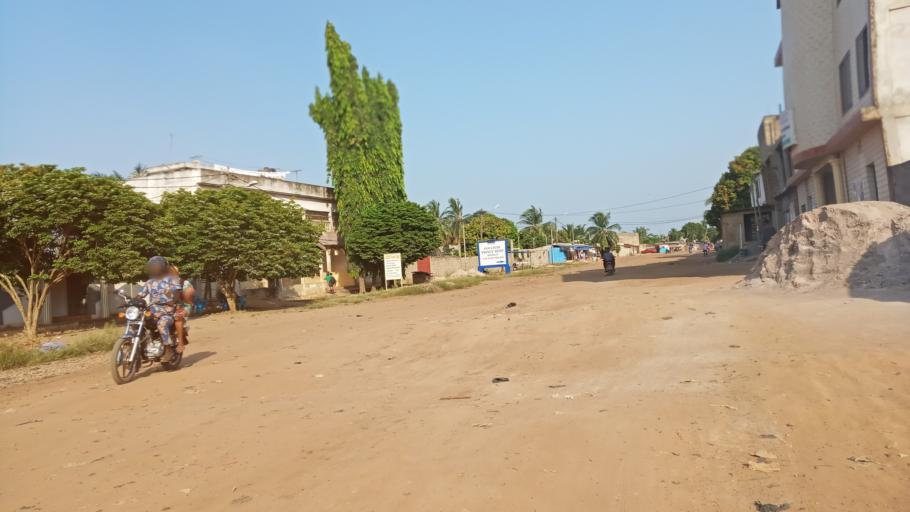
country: TG
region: Maritime
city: Lome
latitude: 6.1813
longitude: 1.1557
